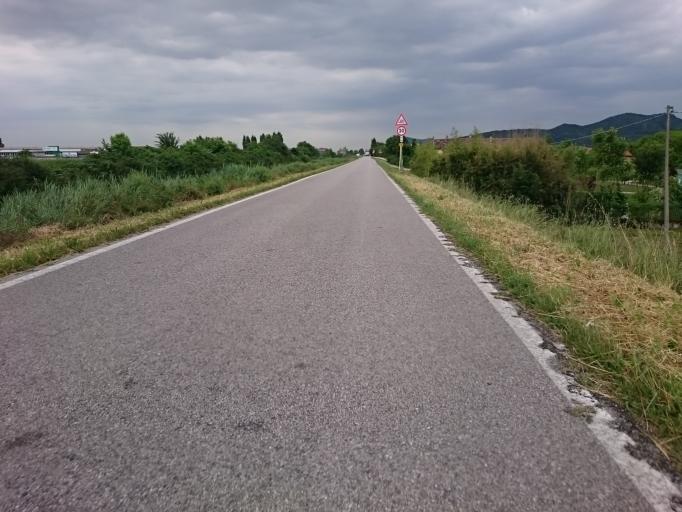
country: IT
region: Veneto
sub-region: Provincia di Padova
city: Terradura
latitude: 45.3275
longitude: 11.8142
